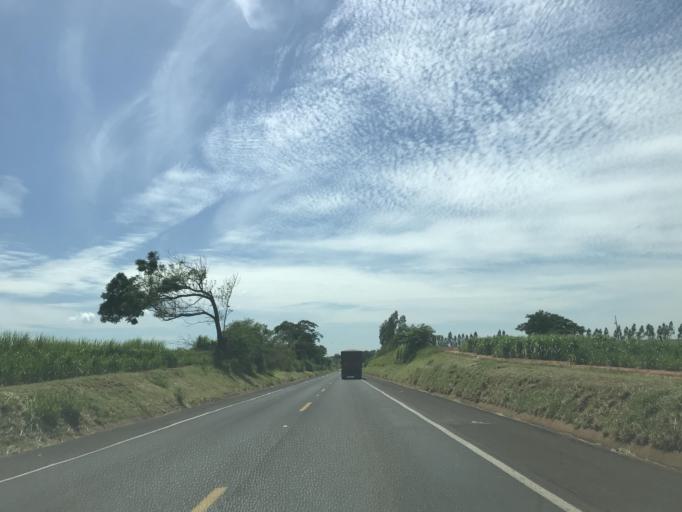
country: BR
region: Parana
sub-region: Paranavai
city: Nova Aurora
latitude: -22.9578
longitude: -52.6731
